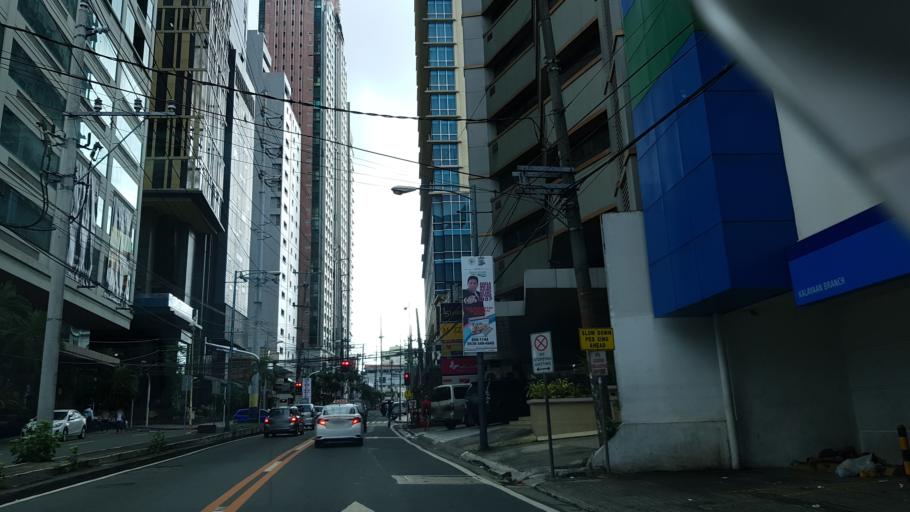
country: PH
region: Metro Manila
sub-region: Makati City
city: Makati City
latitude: 14.5647
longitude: 121.0288
